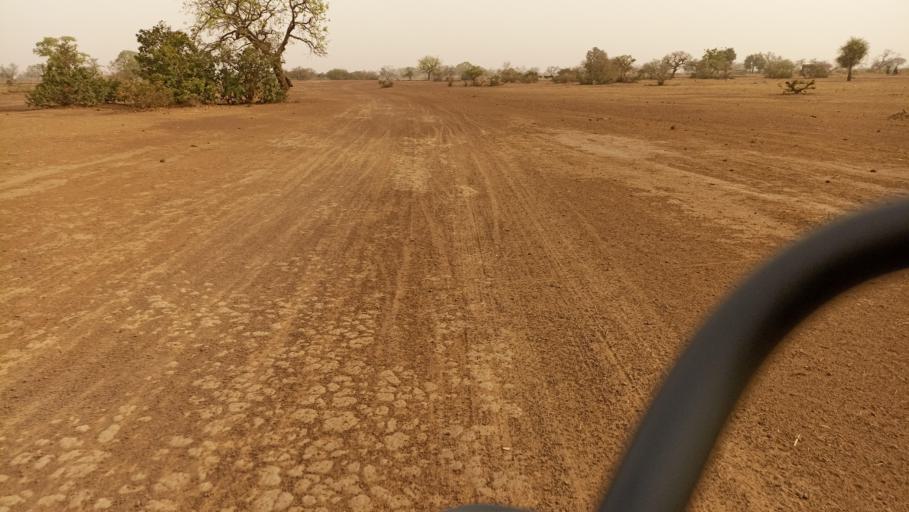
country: BF
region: Nord
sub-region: Province du Zondoma
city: Gourcy
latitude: 13.1440
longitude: -2.5973
